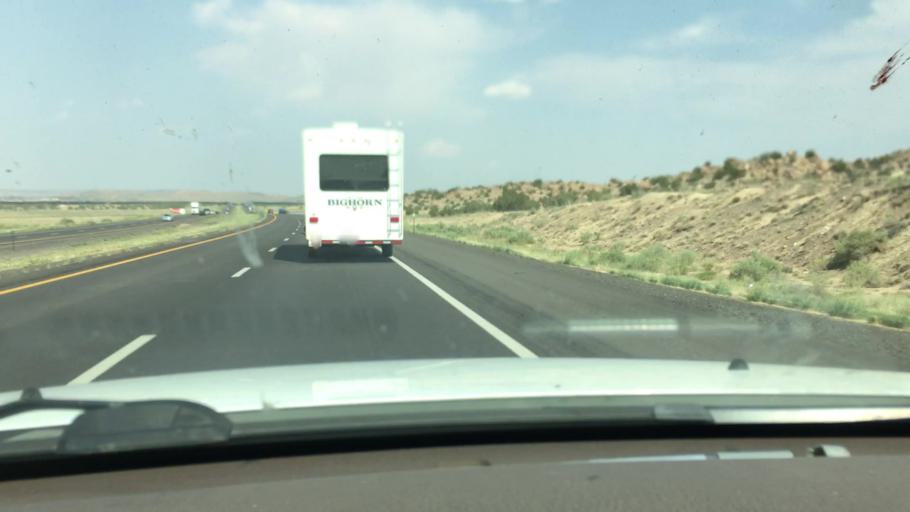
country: US
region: New Mexico
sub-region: Cibola County
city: Laguna
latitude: 35.0271
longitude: -107.4489
